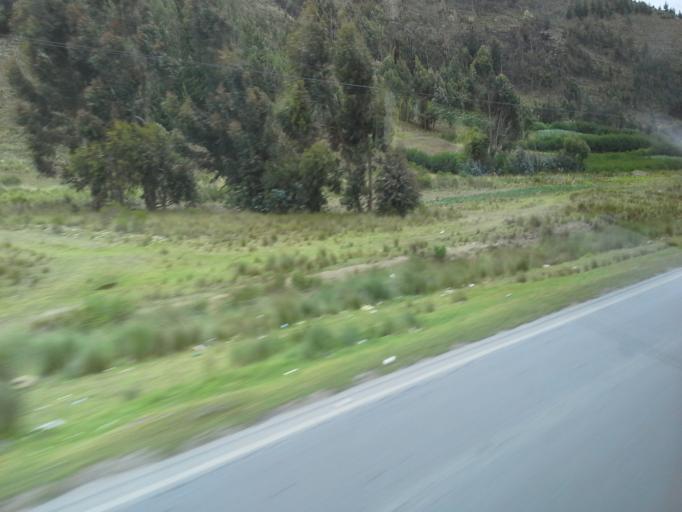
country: BO
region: Cochabamba
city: Colomi
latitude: -17.3795
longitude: -65.8343
